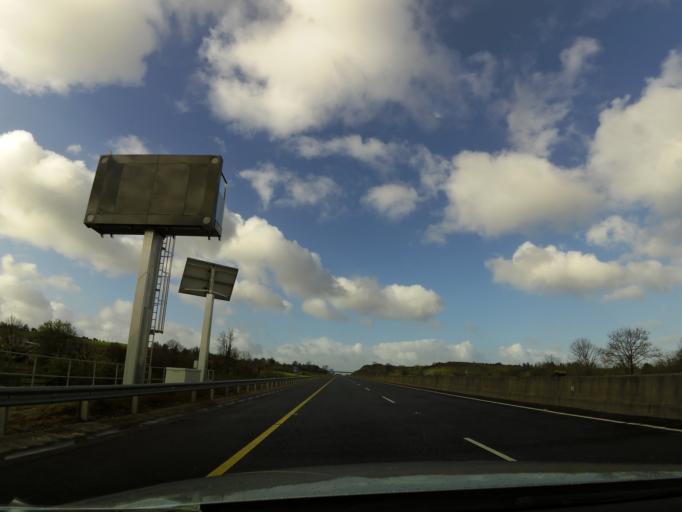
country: IE
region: Munster
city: Ballina
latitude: 52.7772
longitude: -8.3777
